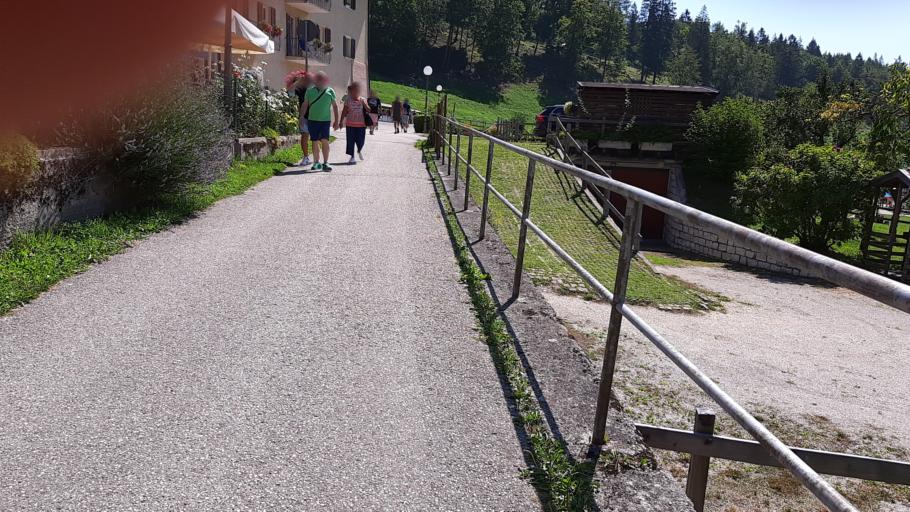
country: IT
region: Trentino-Alto Adige
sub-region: Provincia di Trento
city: Gionghi-Cappella
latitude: 45.9379
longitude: 11.2531
